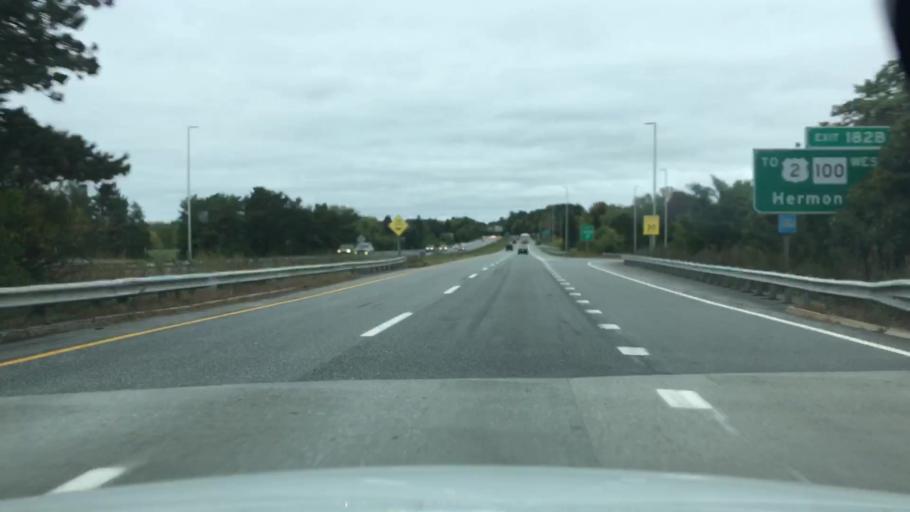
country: US
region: Maine
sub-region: Penobscot County
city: Bangor
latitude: 44.7873
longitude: -68.8080
